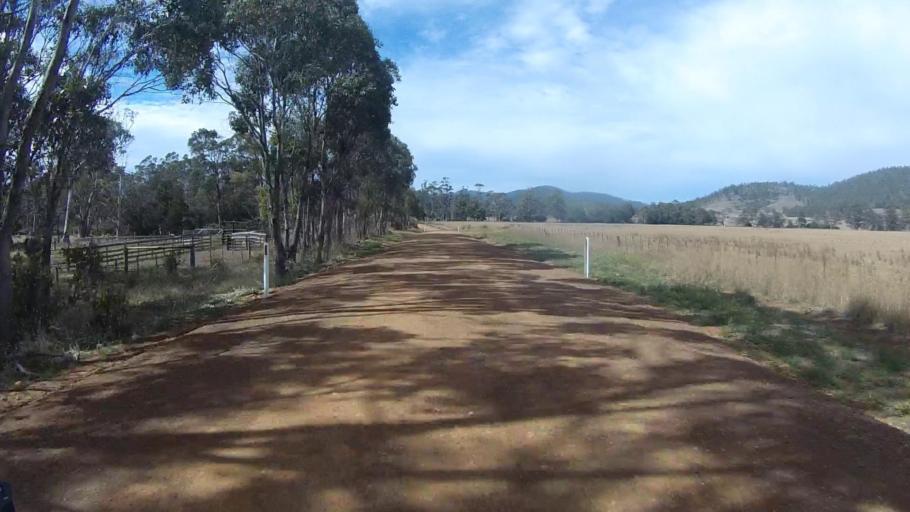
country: AU
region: Tasmania
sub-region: Sorell
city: Sorell
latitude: -42.6376
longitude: 147.9003
